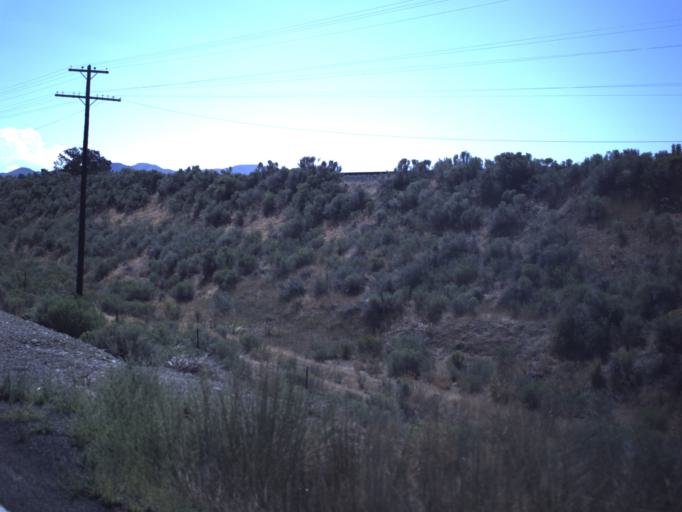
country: US
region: Utah
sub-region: Utah County
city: Genola
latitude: 39.9450
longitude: -112.2271
